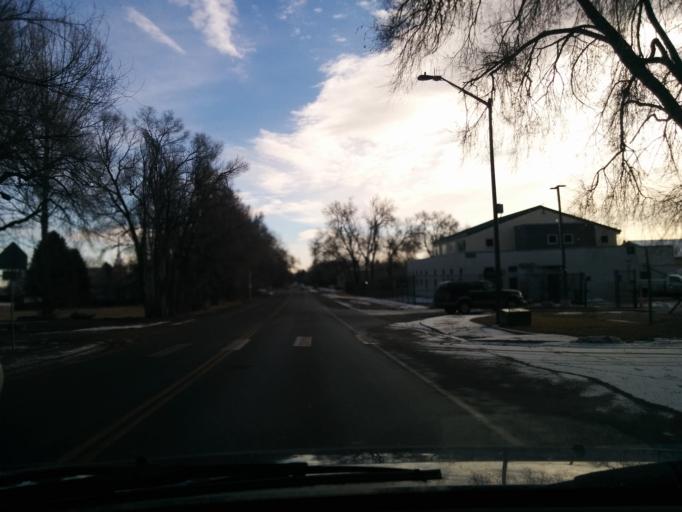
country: US
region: Colorado
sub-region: Larimer County
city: Laporte
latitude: 40.5893
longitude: -105.1240
